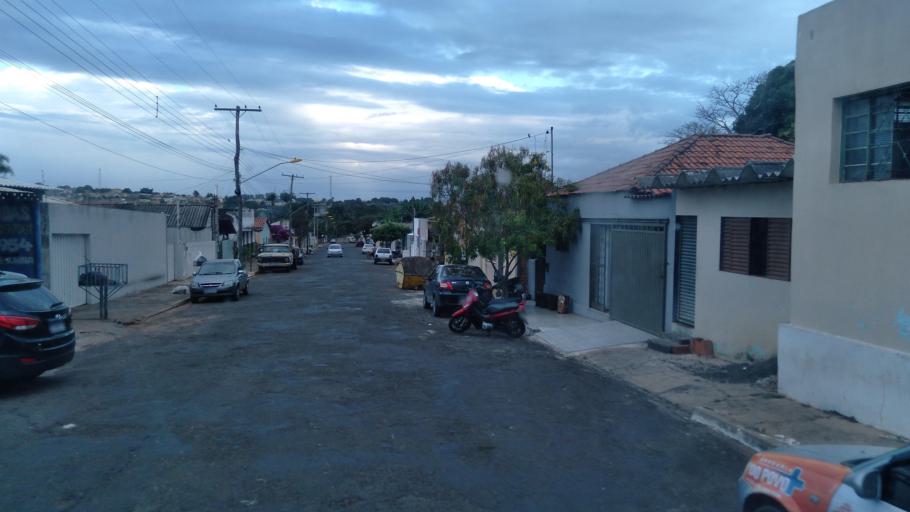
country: BR
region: Goias
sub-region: Mineiros
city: Mineiros
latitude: -17.5658
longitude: -52.5485
